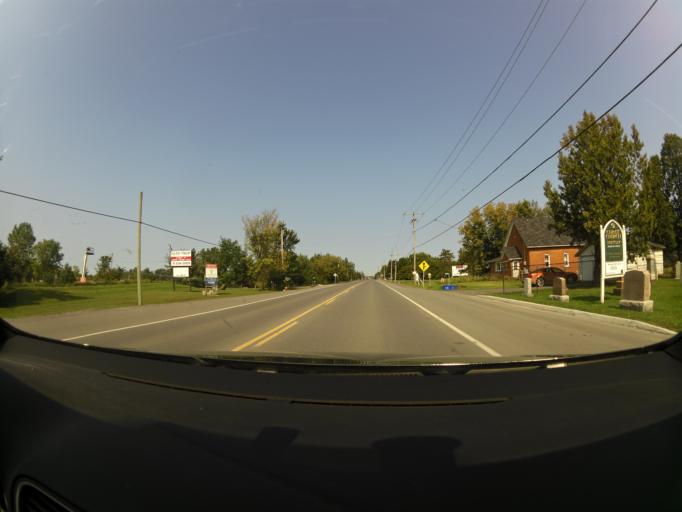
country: CA
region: Ontario
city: Bells Corners
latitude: 45.3141
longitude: -75.9979
